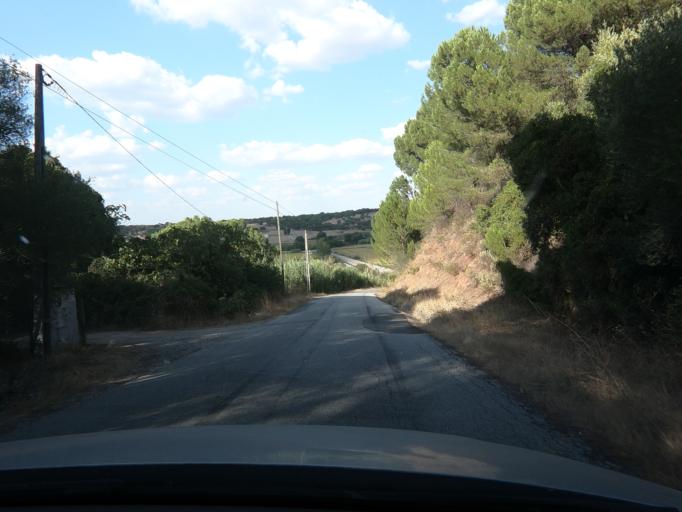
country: PT
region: Setubal
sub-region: Alcacer do Sal
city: Alcacer do Sal
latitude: 38.2464
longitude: -8.3606
